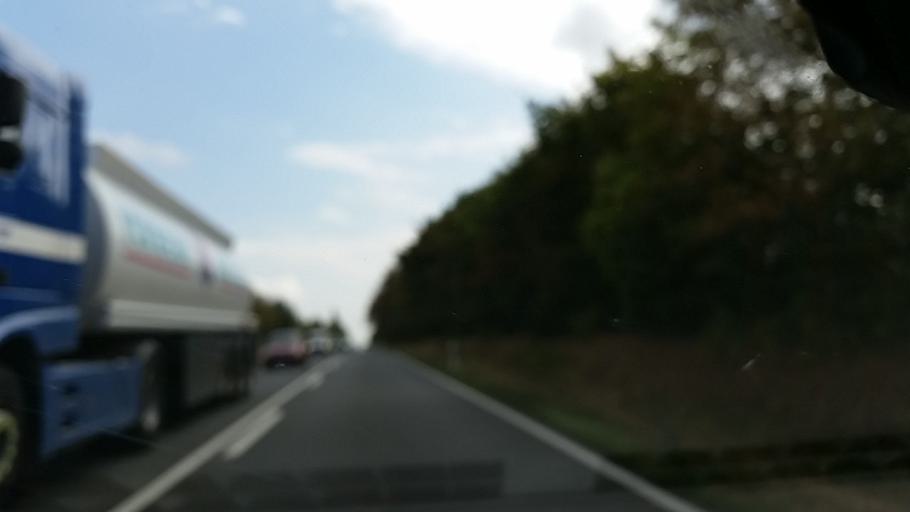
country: DE
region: Saxony-Anhalt
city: Querfurt
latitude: 51.3654
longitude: 11.6132
